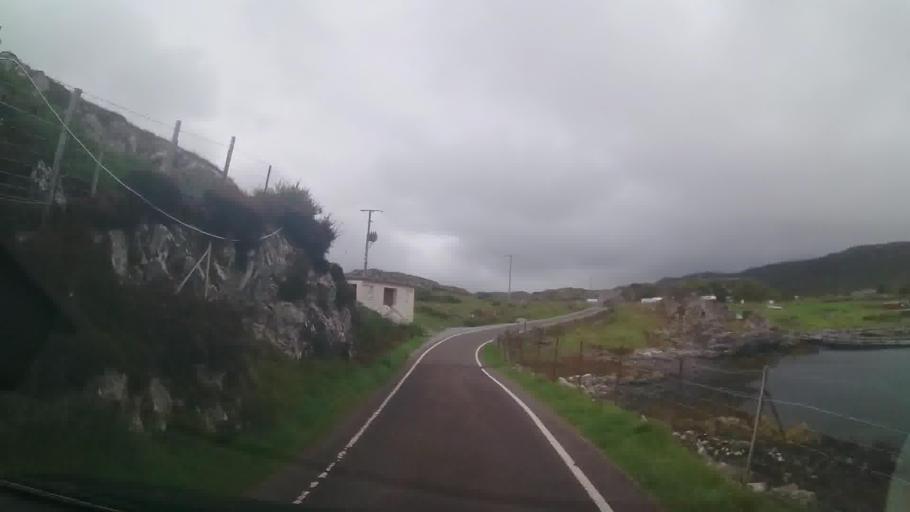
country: GB
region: Scotland
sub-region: Argyll and Bute
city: Isle Of Mull
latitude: 56.6889
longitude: -6.0955
